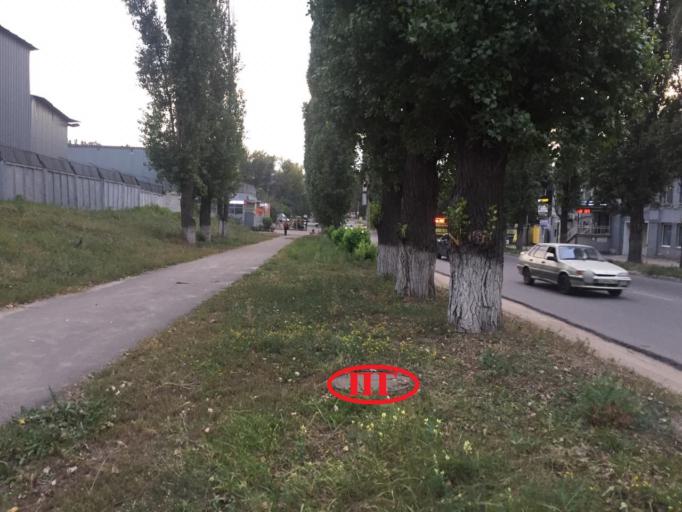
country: RU
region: Voronezj
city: Voronezh
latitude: 51.6810
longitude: 39.1637
